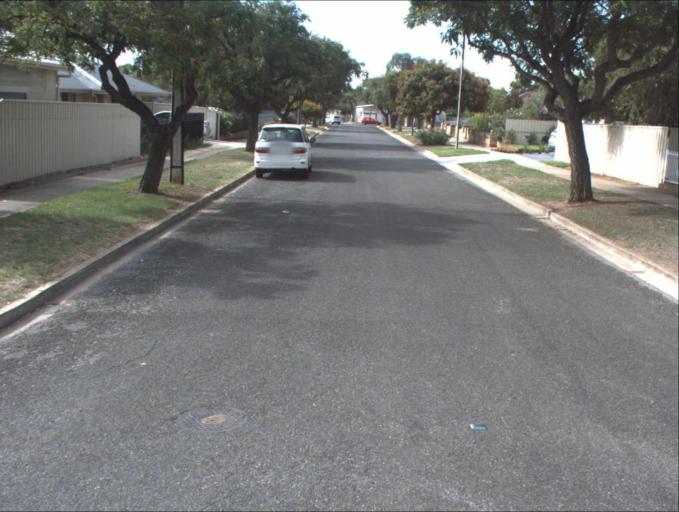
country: AU
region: South Australia
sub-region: Port Adelaide Enfield
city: Blair Athol
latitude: -34.8671
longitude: 138.5939
